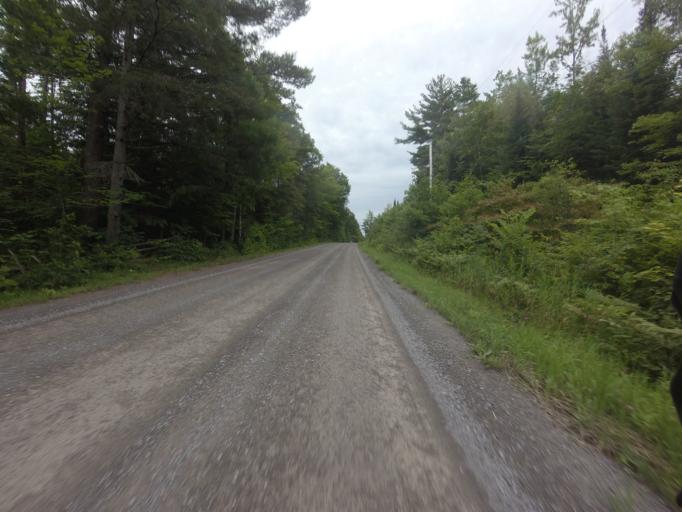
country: CA
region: Ontario
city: Carleton Place
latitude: 45.1567
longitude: -76.2642
